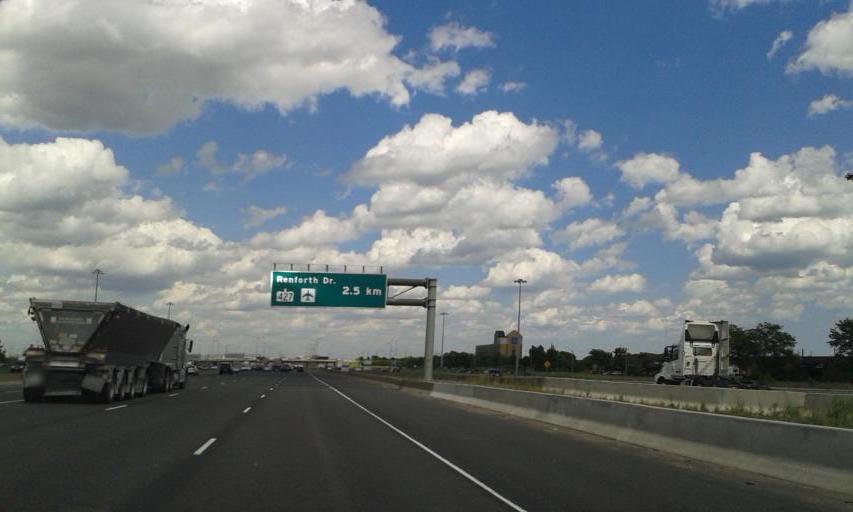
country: CA
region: Ontario
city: Mississauga
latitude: 43.6431
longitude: -79.6505
